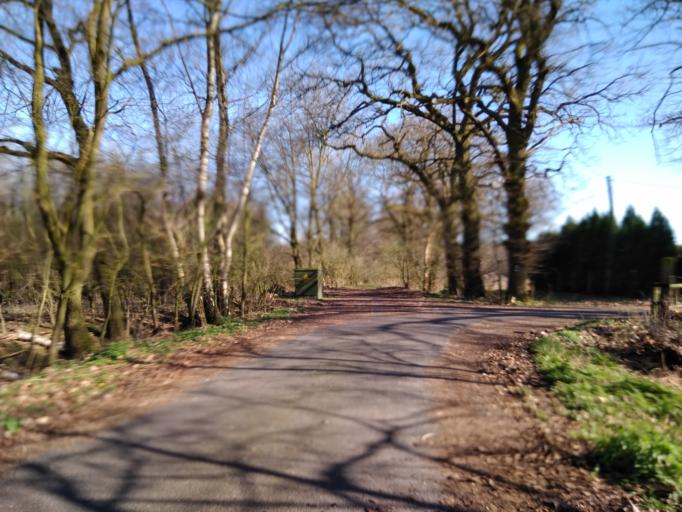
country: DE
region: North Rhine-Westphalia
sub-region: Regierungsbezirk Dusseldorf
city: Schermbeck
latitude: 51.6314
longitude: 6.8440
